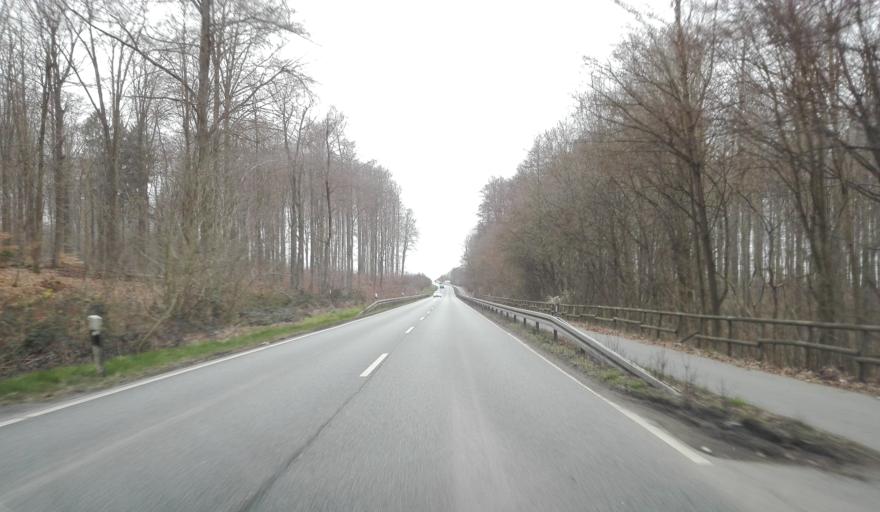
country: DE
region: Hesse
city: Ober-Ramstadt
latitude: 49.8170
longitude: 8.7696
